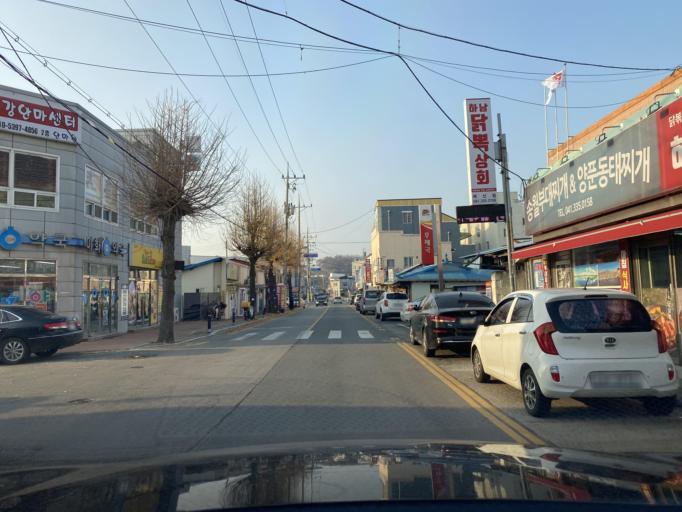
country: KR
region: Chungcheongnam-do
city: Yesan
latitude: 36.6877
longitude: 126.8311
